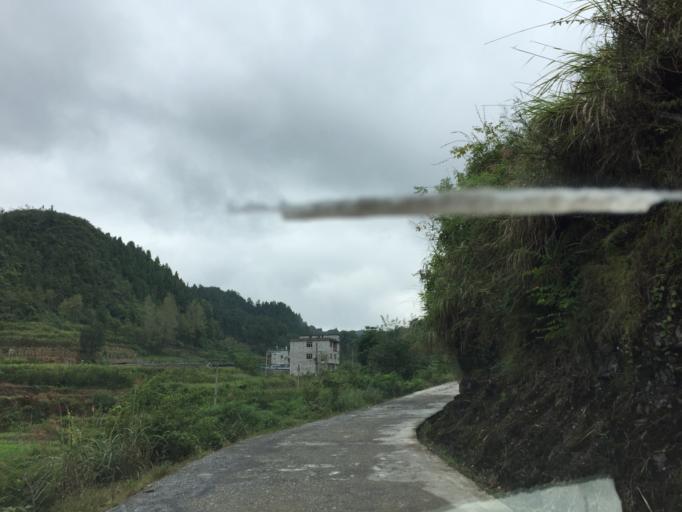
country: CN
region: Guizhou Sheng
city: Longquan
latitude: 28.2025
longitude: 108.0538
